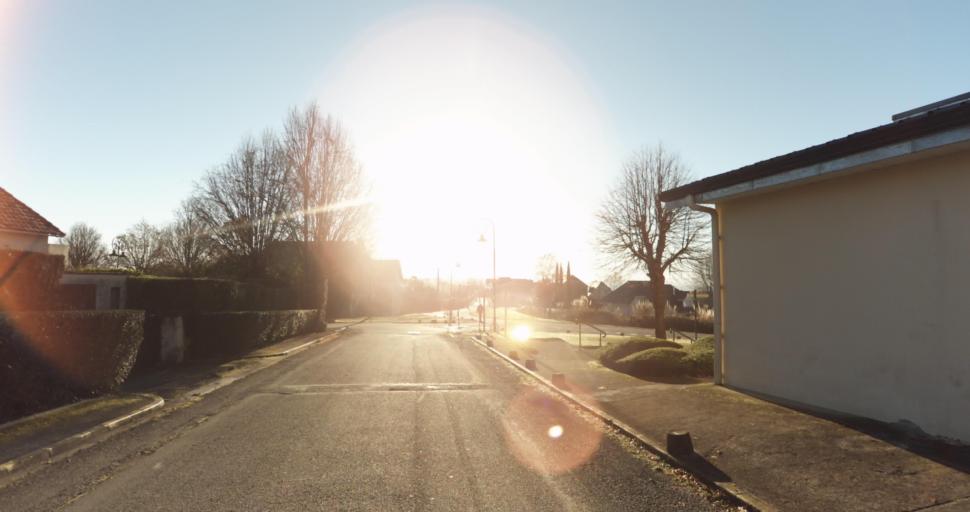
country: FR
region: Aquitaine
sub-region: Departement des Pyrenees-Atlantiques
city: Morlaas
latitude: 43.3252
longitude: -0.2566
